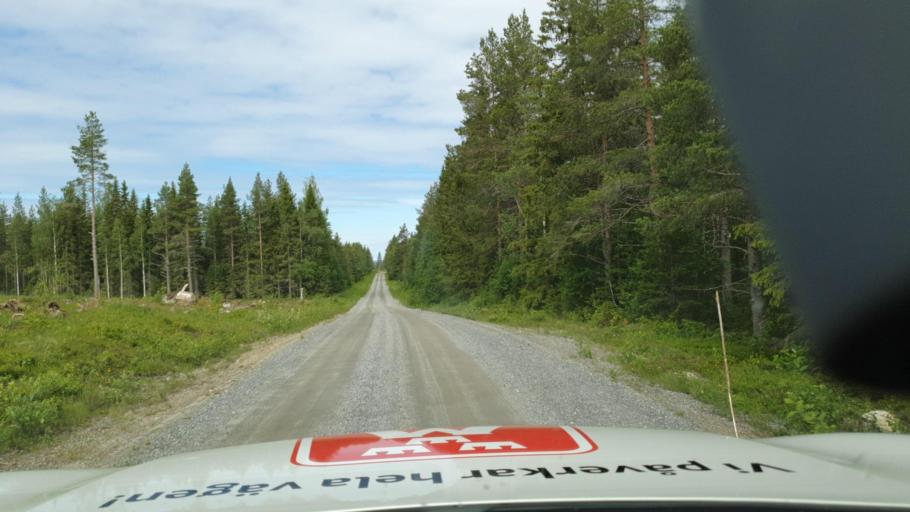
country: SE
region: Vaesterbotten
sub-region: Skelleftea Kommun
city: Langsele
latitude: 64.6251
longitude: 20.2569
